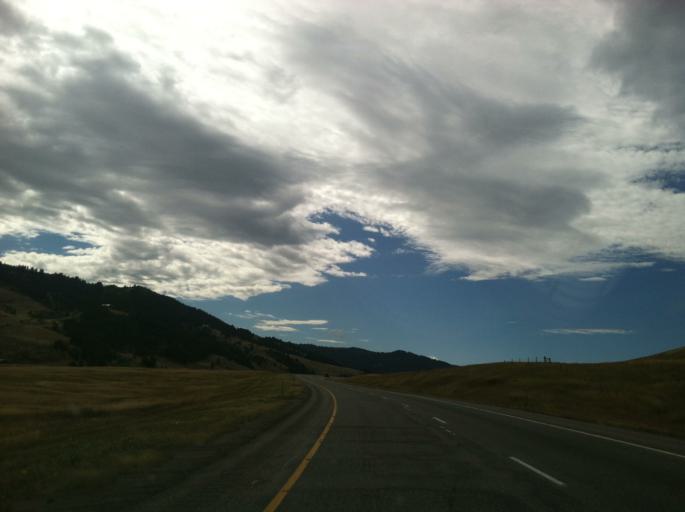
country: US
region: Montana
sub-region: Park County
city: Livingston
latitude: 45.6632
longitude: -110.7206
